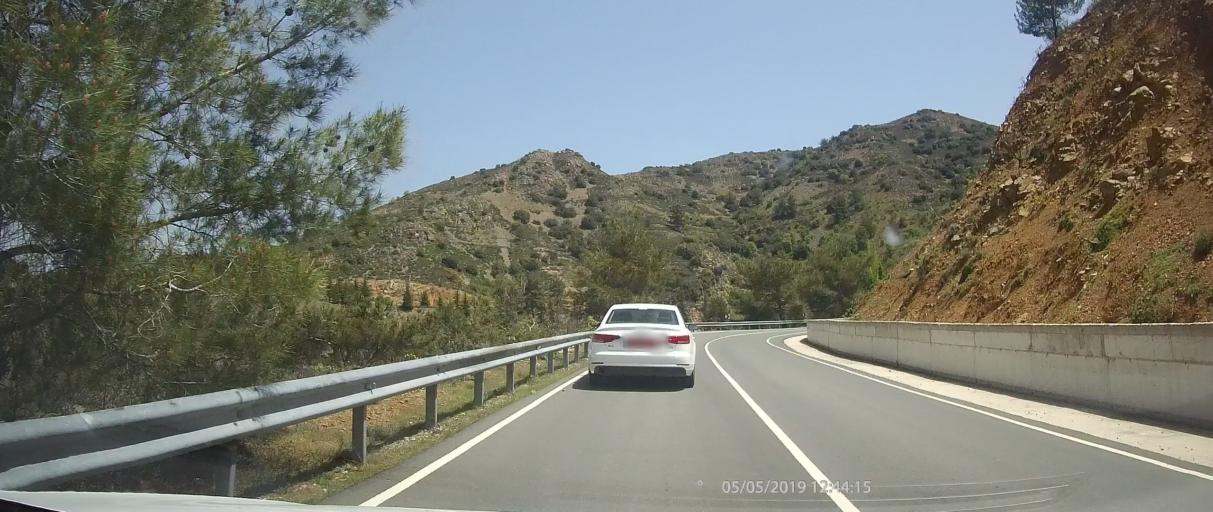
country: CY
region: Lefkosia
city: Kakopetria
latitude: 34.9674
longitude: 32.8194
